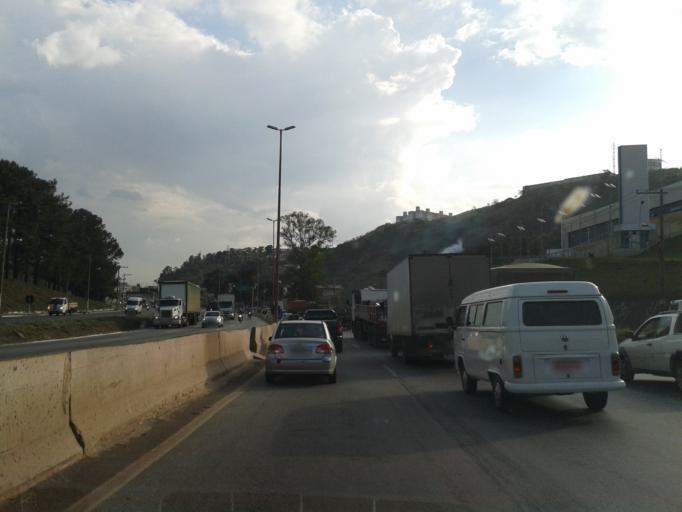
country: BR
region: Minas Gerais
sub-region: Belo Horizonte
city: Belo Horizonte
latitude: -19.8930
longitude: -43.9780
